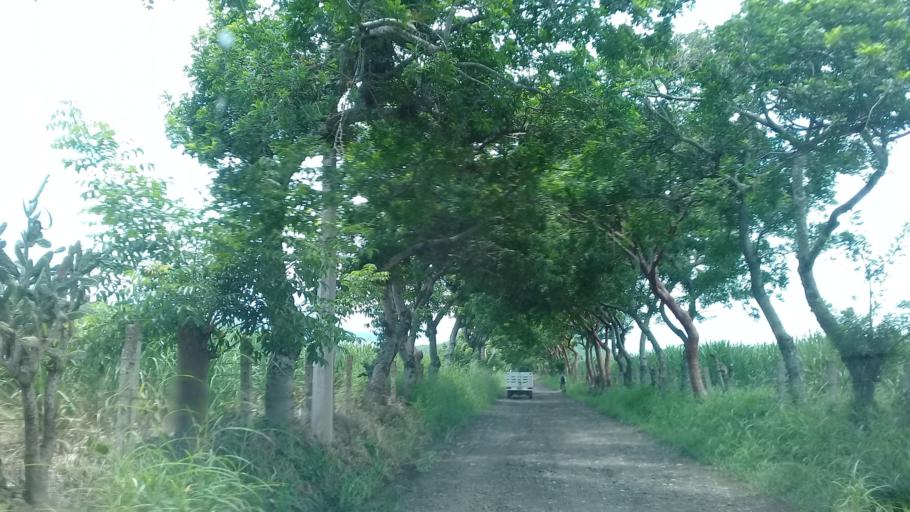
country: MX
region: Veracruz
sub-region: Naolinco
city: El Espinal
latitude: 19.5884
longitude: -96.8629
